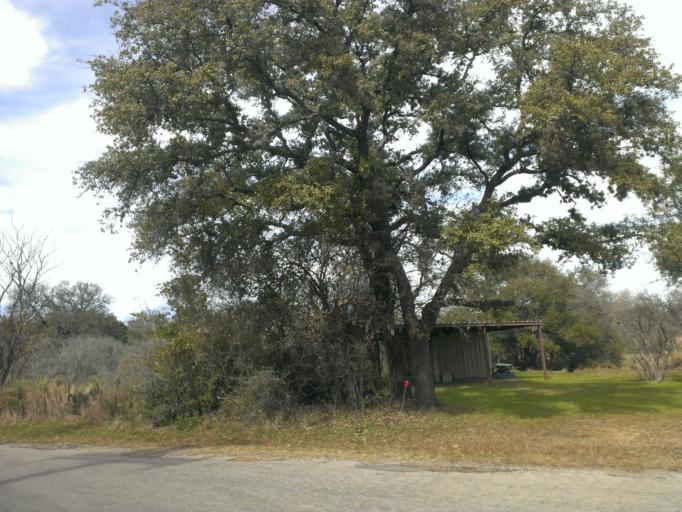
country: US
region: Texas
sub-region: Burnet County
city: Granite Shoals
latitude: 30.5783
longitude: -98.3900
